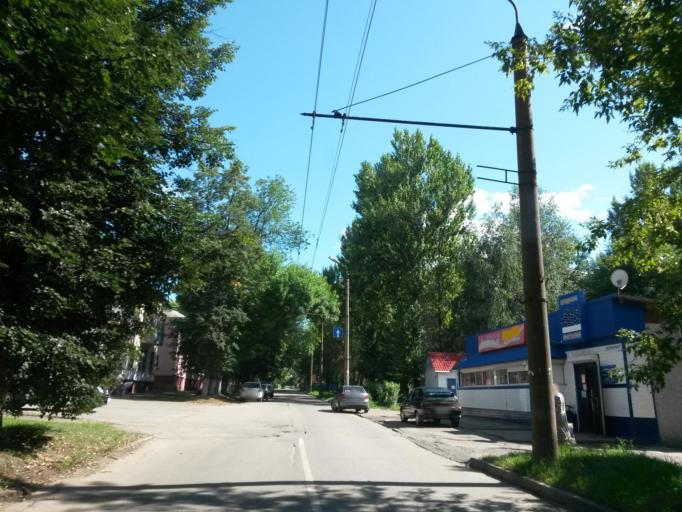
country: RU
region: Jaroslavl
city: Yaroslavl
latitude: 57.5806
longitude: 39.8384
